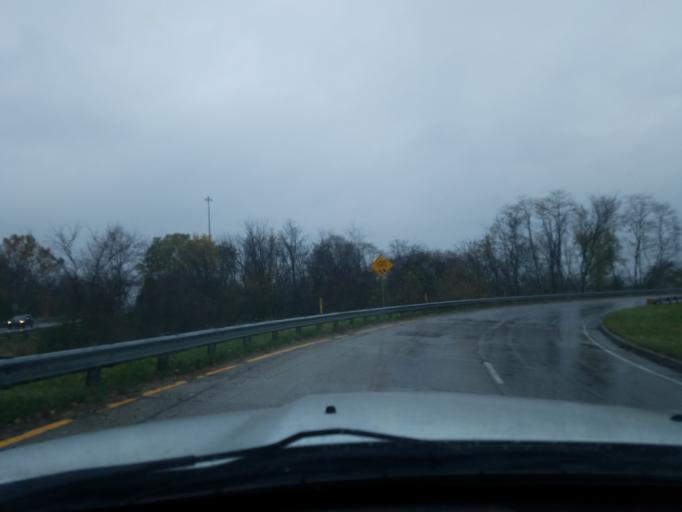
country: US
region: Indiana
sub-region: Floyd County
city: New Albany
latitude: 38.2844
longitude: -85.8303
